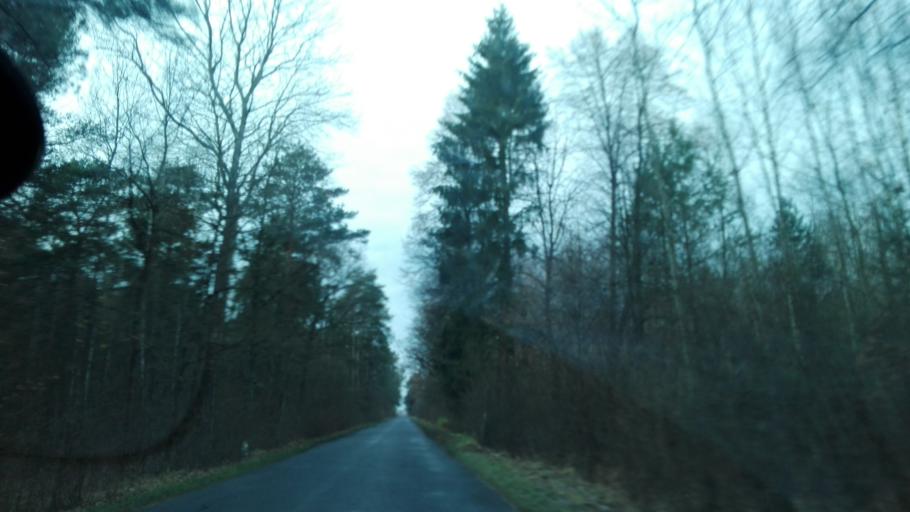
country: PL
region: Lublin Voivodeship
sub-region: Powiat bialski
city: Sosnowka
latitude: 51.7463
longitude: 23.3612
